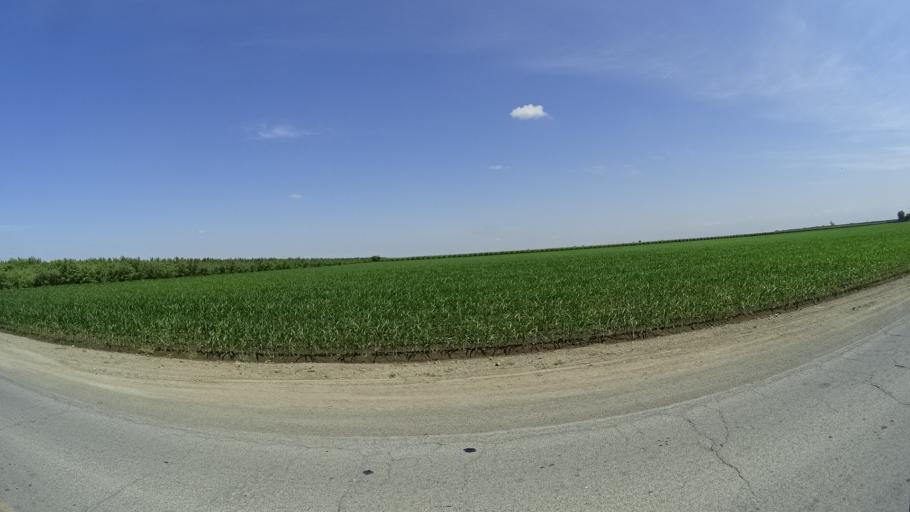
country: US
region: California
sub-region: Tulare County
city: Goshen
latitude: 36.2691
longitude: -119.5008
